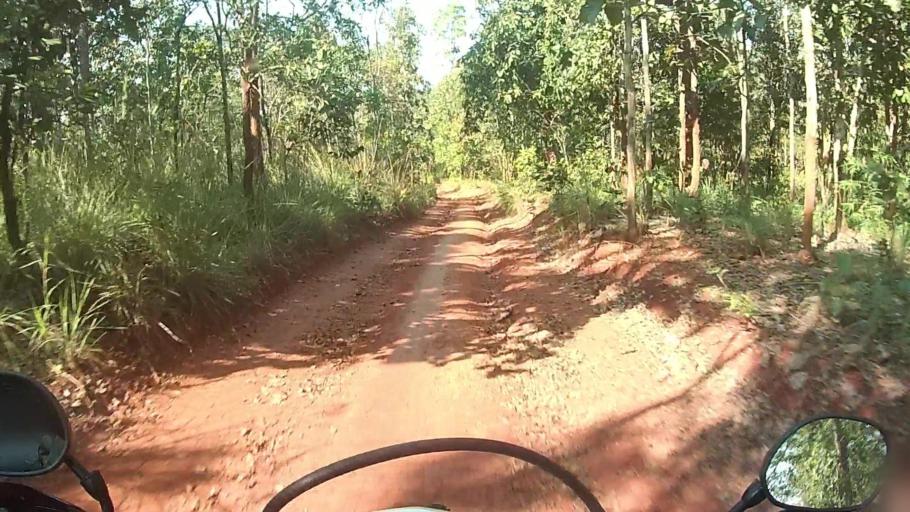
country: TH
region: Chiang Mai
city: Mae On
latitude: 18.9204
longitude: 99.2120
